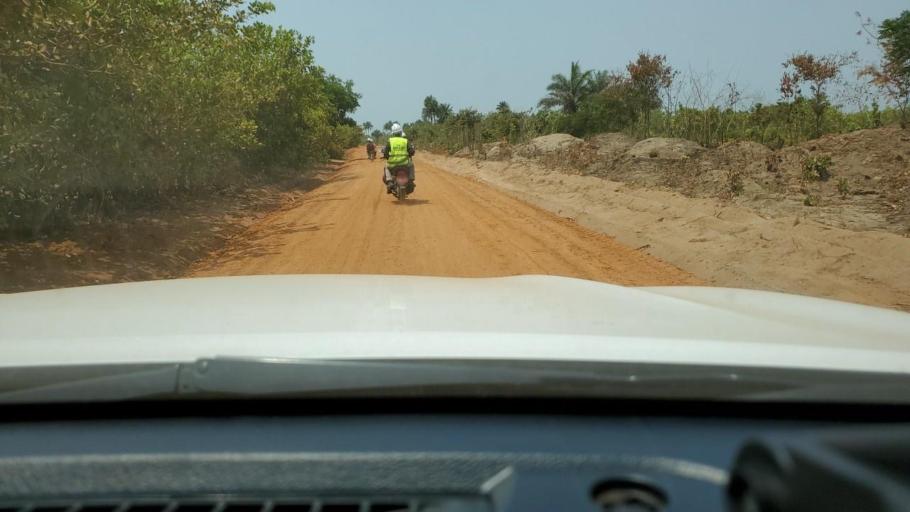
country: GN
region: Boke
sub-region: Boffa
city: Boffa
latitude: 10.0651
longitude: -13.8681
